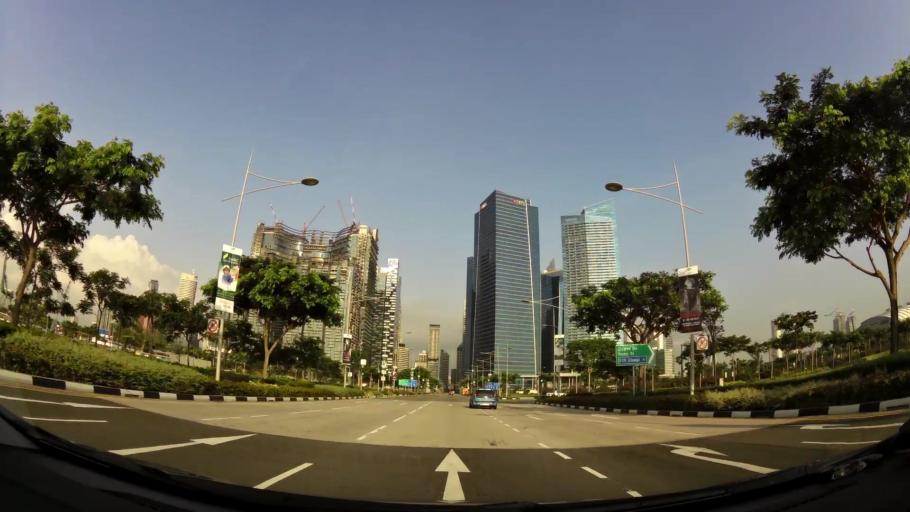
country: SG
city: Singapore
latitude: 1.2763
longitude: 103.8580
